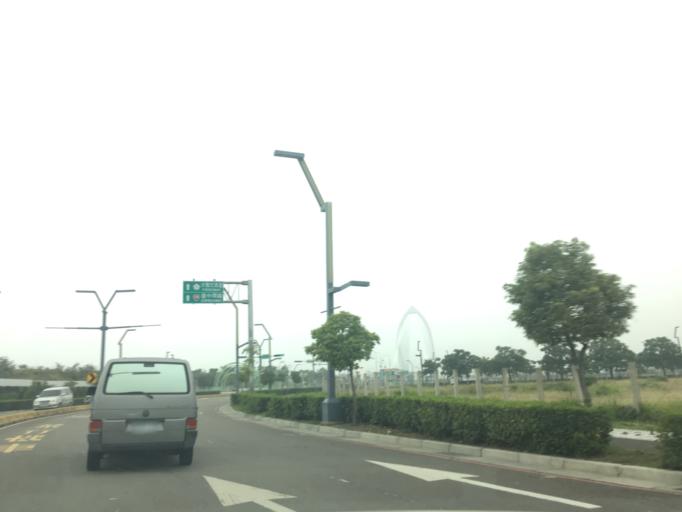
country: TW
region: Taiwan
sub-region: Taichung City
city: Taichung
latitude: 24.1946
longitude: 120.6541
